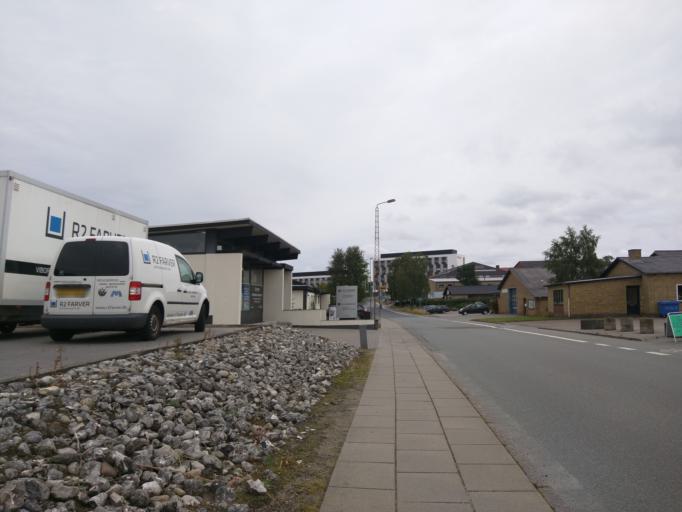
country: DK
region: Central Jutland
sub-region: Viborg Kommune
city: Viborg
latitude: 56.4474
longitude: 9.3889
